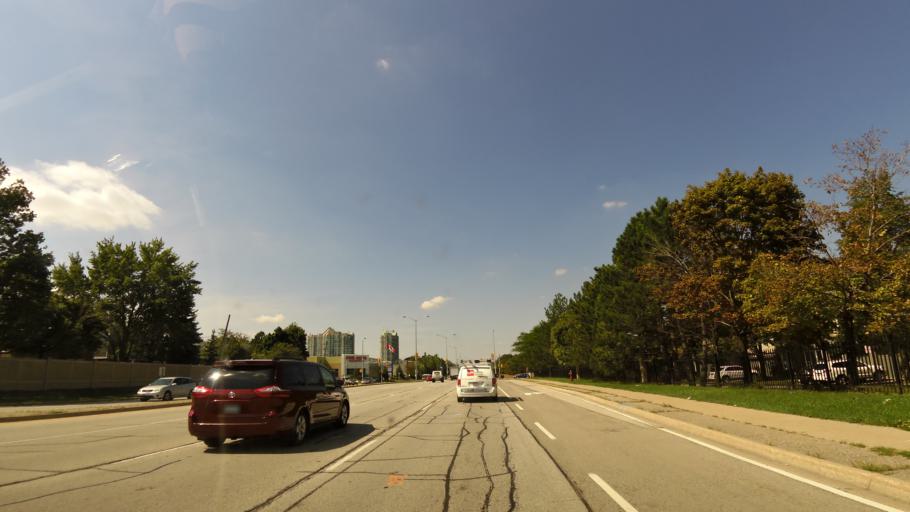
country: CA
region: Ontario
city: Mississauga
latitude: 43.5433
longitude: -79.6787
